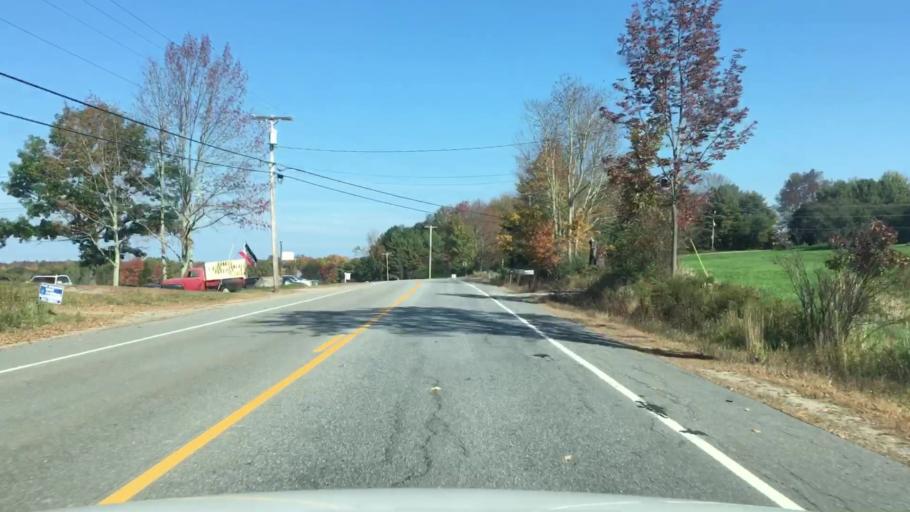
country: US
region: Maine
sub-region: Sagadahoc County
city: Topsham
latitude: 44.0246
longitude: -69.9421
